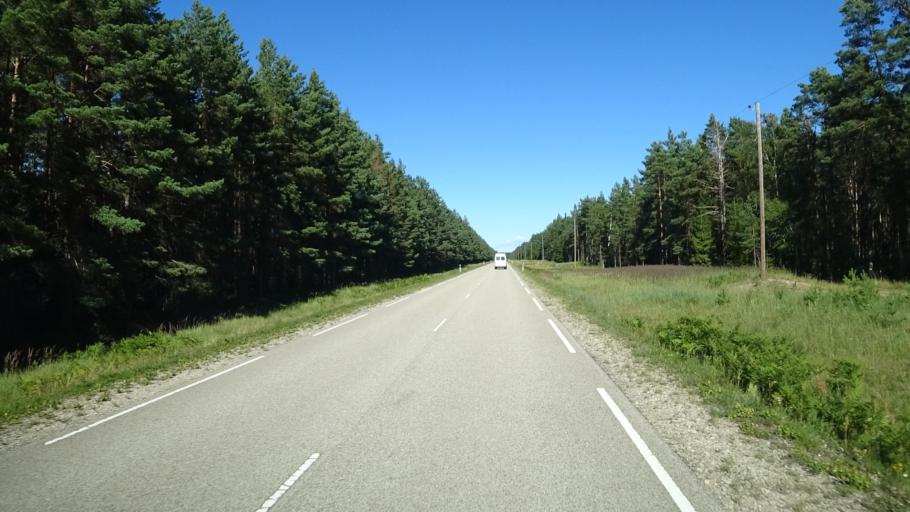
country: LV
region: Dundaga
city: Dundaga
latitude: 57.7285
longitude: 22.5023
